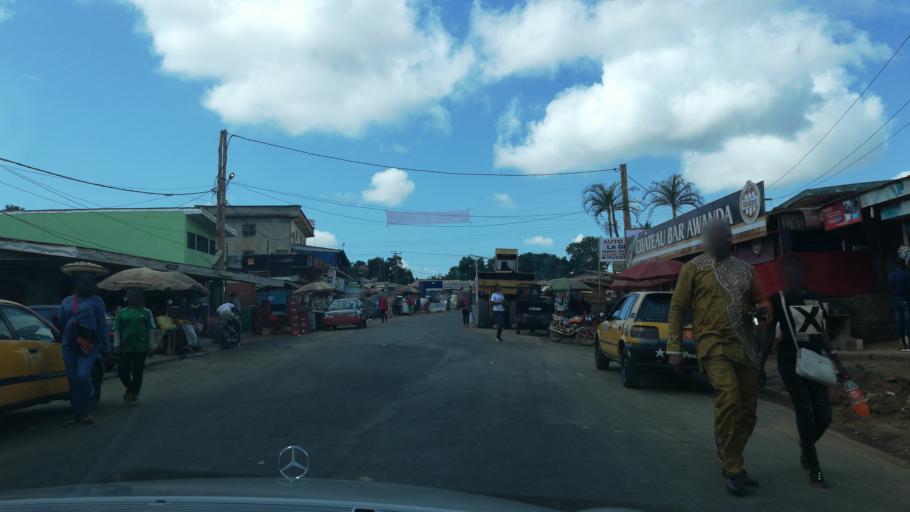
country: CM
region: Centre
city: Yaounde
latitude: 3.8212
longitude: 11.5078
